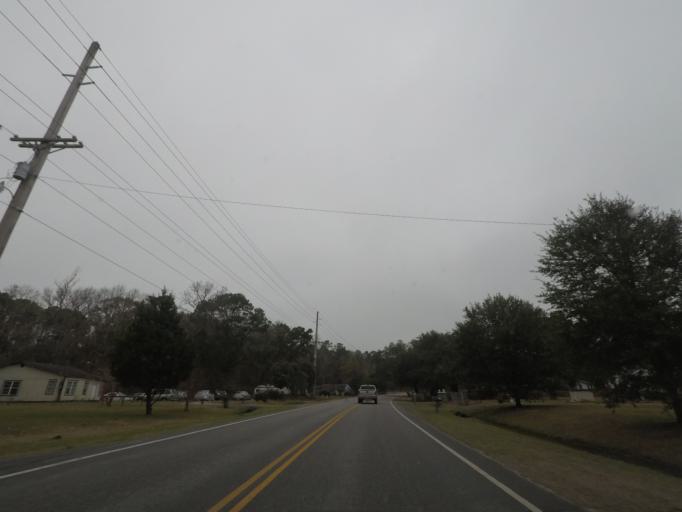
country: US
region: South Carolina
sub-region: Charleston County
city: Meggett
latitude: 32.5849
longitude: -80.3464
